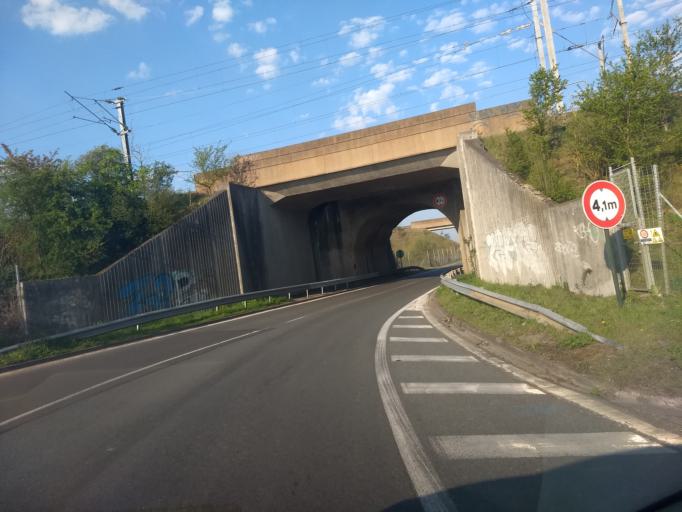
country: FR
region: Nord-Pas-de-Calais
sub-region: Departement du Pas-de-Calais
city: Agny
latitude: 50.2422
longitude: 2.7665
